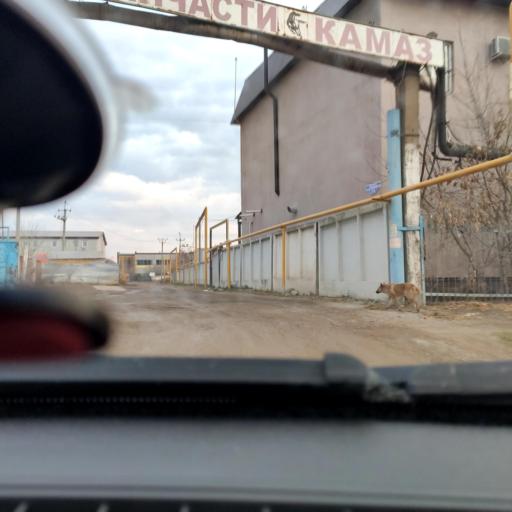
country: RU
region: Bashkortostan
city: Ufa
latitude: 54.7464
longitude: 55.9226
